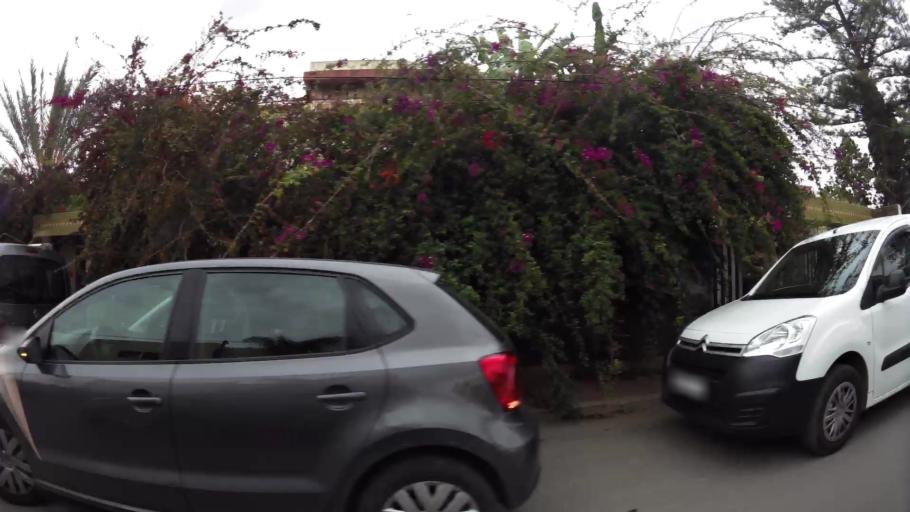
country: MA
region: Grand Casablanca
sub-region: Casablanca
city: Casablanca
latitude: 33.5681
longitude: -7.6203
